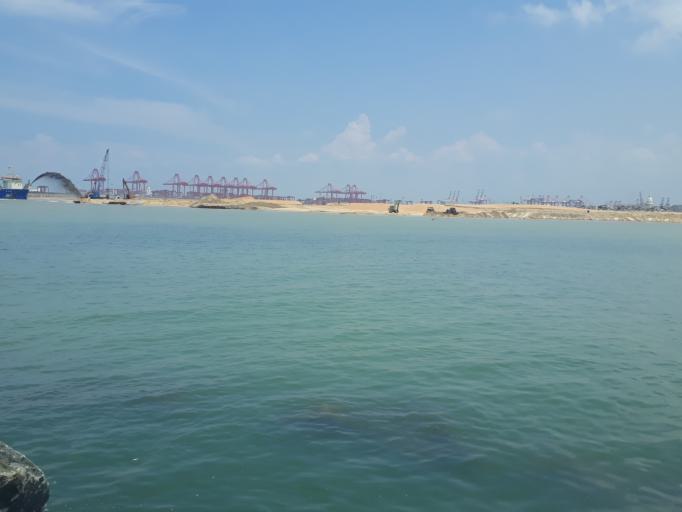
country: LK
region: Western
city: Colombo
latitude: 6.9281
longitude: 79.8217
